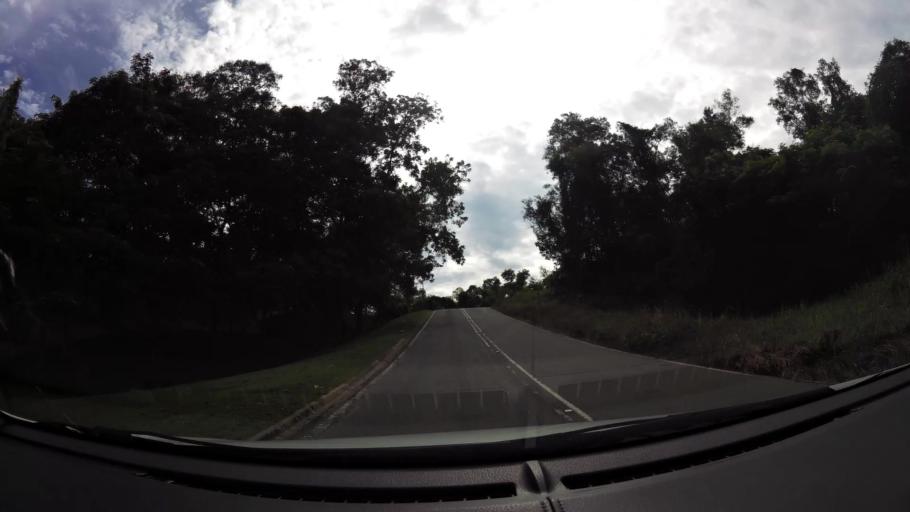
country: BN
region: Brunei and Muara
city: Bandar Seri Begawan
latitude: 4.8915
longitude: 114.8950
